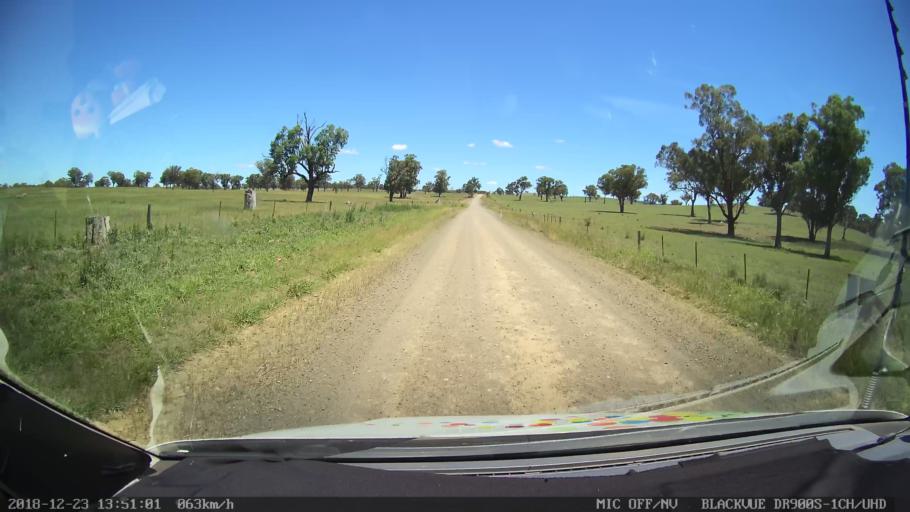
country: AU
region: New South Wales
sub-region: Tamworth Municipality
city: Manilla
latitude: -30.5358
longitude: 151.1057
